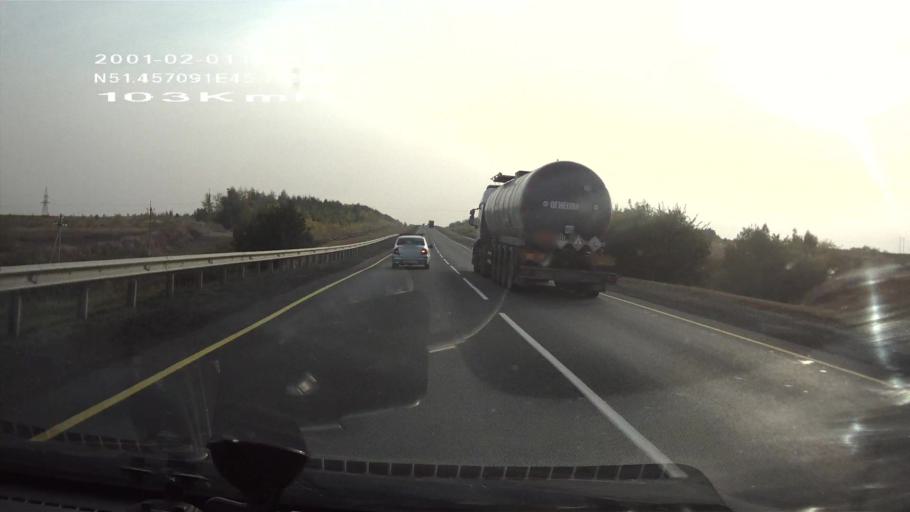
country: RU
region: Saratov
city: Krasnyy Oktyabr'
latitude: 51.4564
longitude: 45.7641
